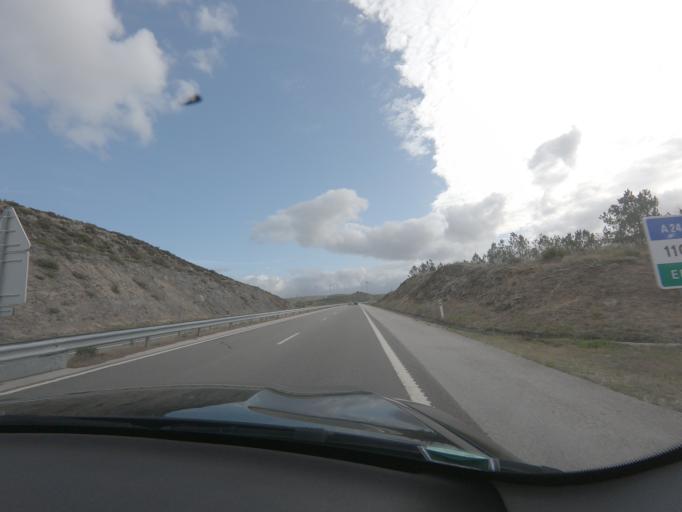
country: PT
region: Viseu
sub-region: Lamego
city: Lamego
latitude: 41.0400
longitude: -7.8597
